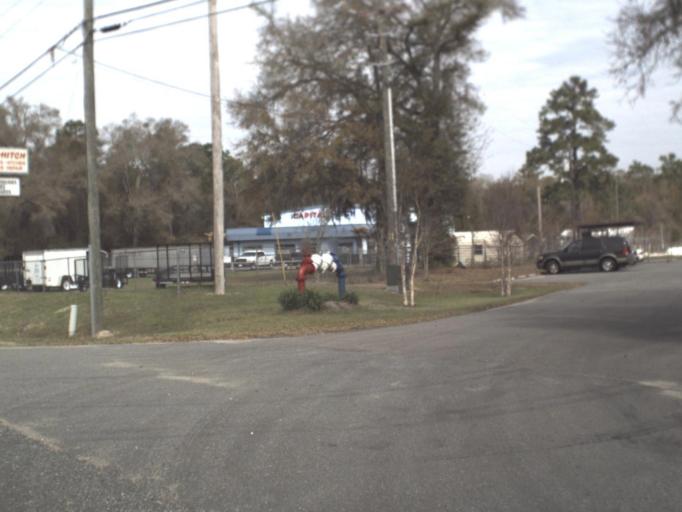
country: US
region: Florida
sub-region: Gadsden County
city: Midway
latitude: 30.4590
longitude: -84.3859
